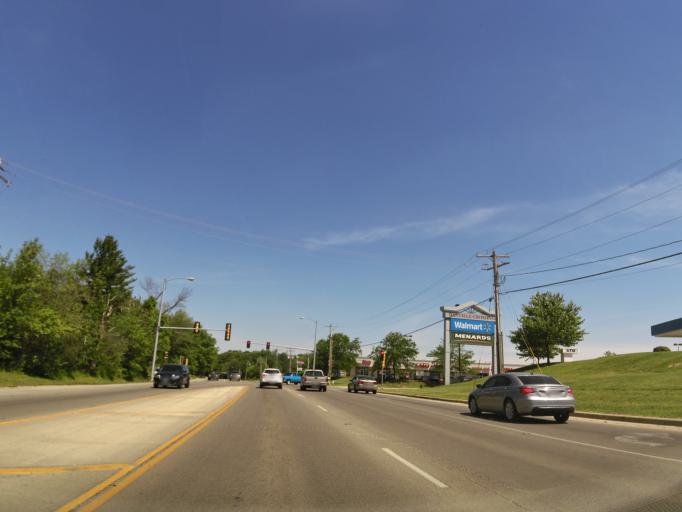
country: US
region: Illinois
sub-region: Vermilion County
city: Danville
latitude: 40.2013
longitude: -87.6301
